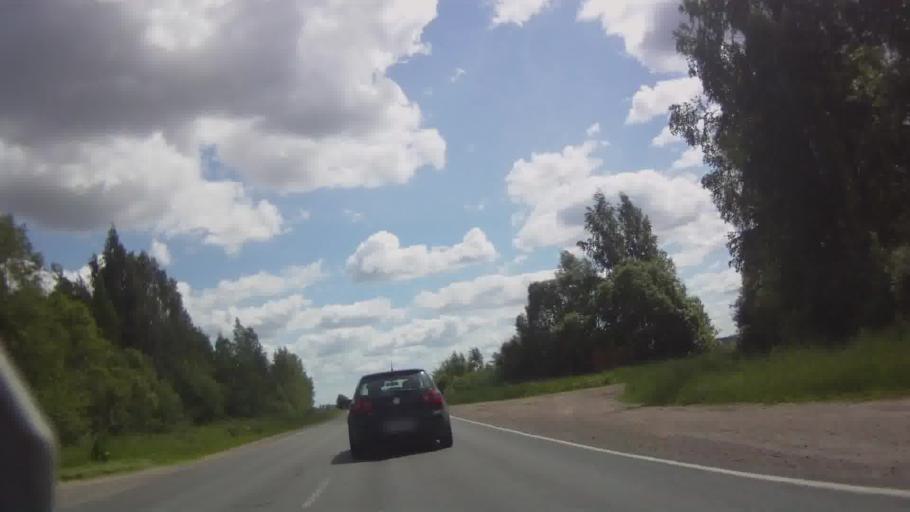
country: LV
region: Vilanu
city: Vilani
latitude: 56.6044
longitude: 26.8533
